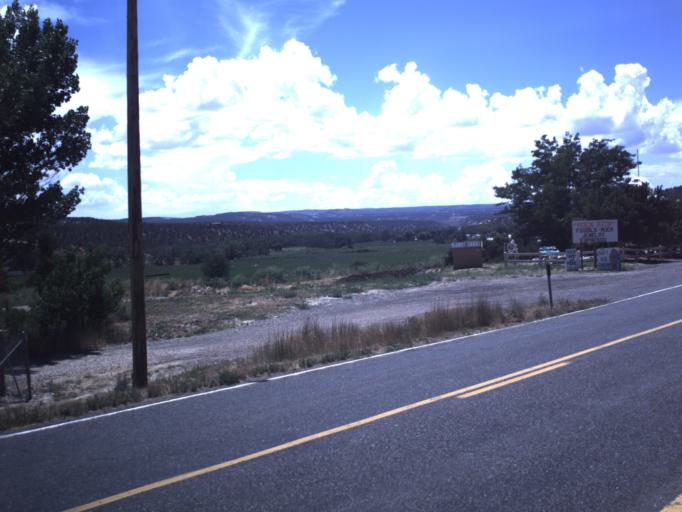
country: US
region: Utah
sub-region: Kane County
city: Kanab
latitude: 37.2726
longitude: -112.6473
